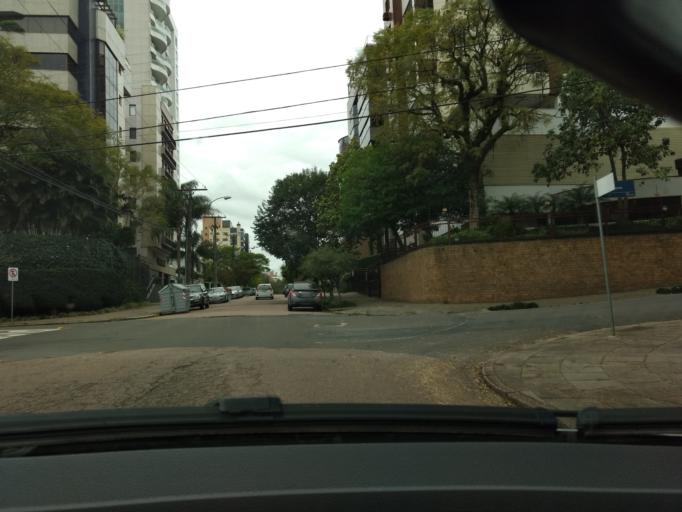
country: BR
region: Rio Grande do Sul
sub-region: Porto Alegre
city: Porto Alegre
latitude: -30.0313
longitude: -51.1811
